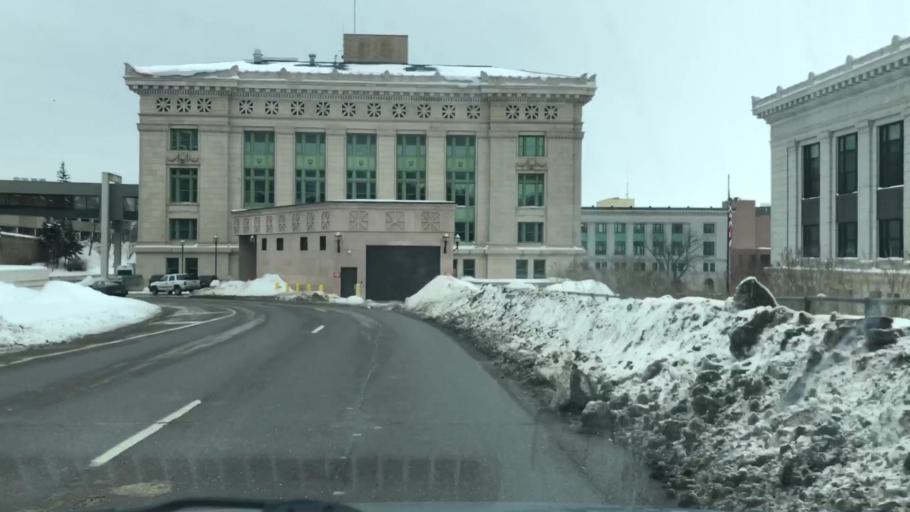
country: US
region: Minnesota
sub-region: Saint Louis County
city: Duluth
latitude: 46.7827
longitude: -92.1076
